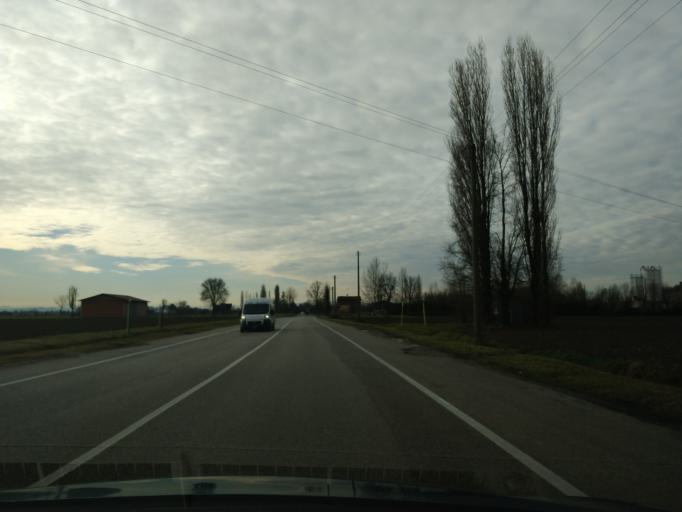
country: IT
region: Emilia-Romagna
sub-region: Provincia di Bologna
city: Argelato
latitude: 44.6549
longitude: 11.3238
